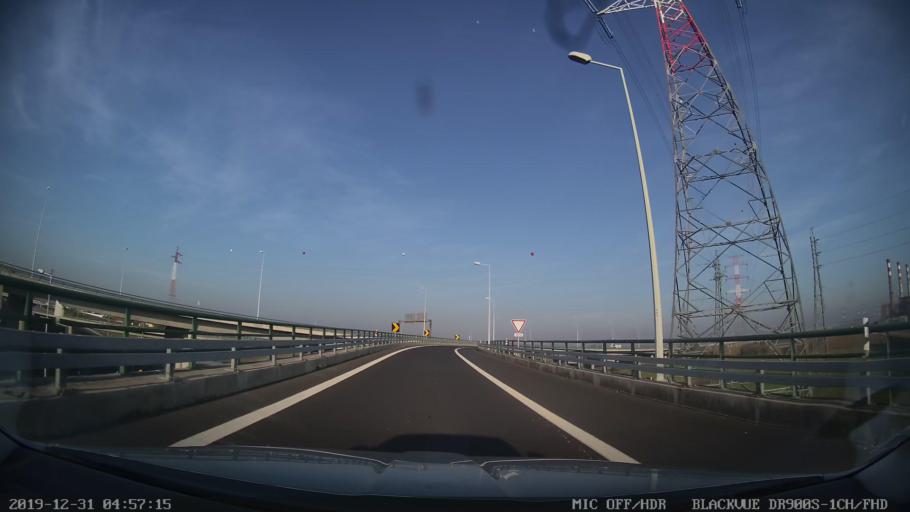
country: PT
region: Lisbon
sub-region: Alenquer
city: Carregado
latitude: 39.0164
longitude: -8.9635
